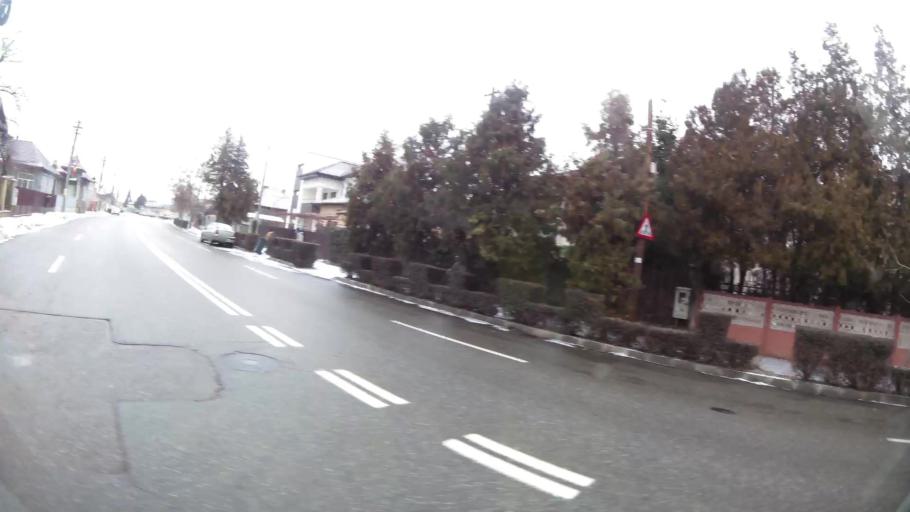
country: RO
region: Dambovita
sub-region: Municipiul Targoviste
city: Targoviste
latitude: 44.9360
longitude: 25.4499
